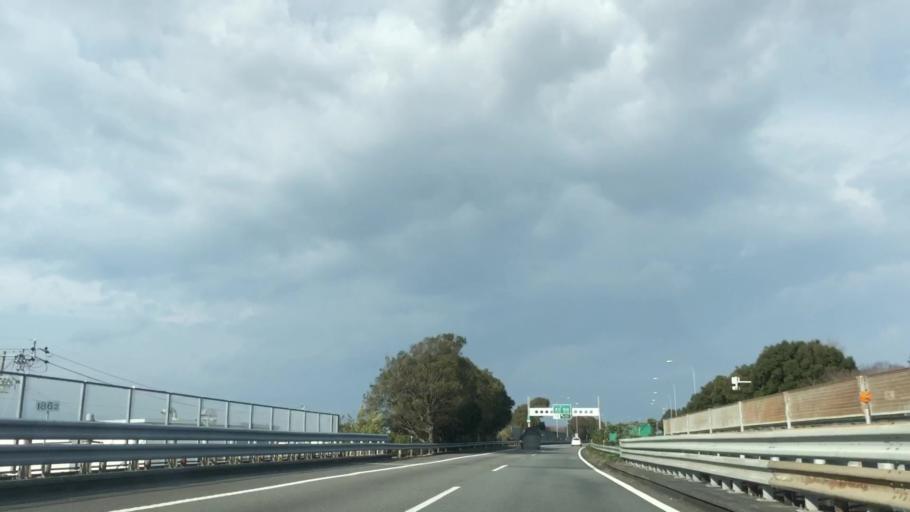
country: JP
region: Shizuoka
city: Shimada
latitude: 34.7869
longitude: 138.2310
